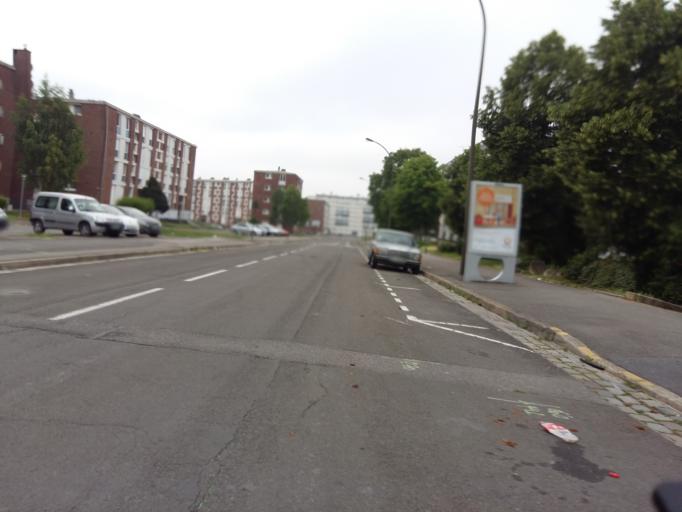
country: FR
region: Picardie
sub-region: Departement de la Somme
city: Amiens
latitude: 49.9098
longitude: 2.3005
